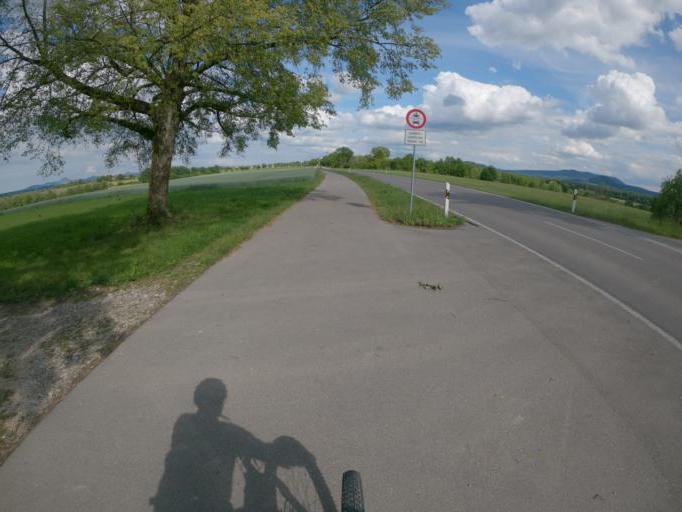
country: DE
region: Baden-Wuerttemberg
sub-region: Regierungsbezirk Stuttgart
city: Hattenhofen
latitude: 48.6643
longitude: 9.5505
